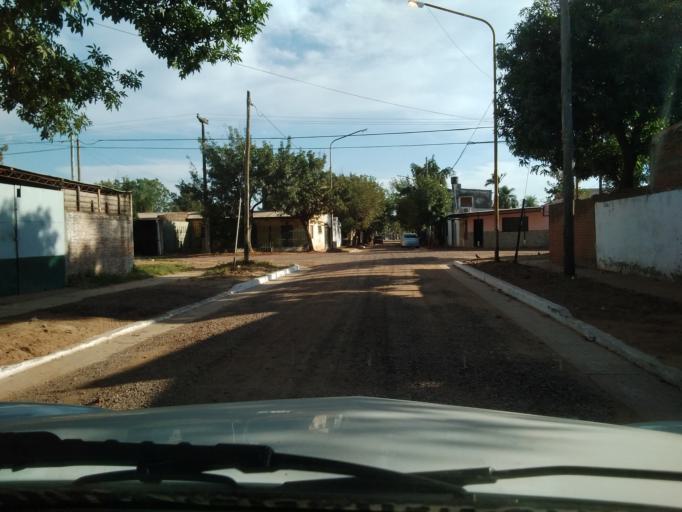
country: AR
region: Corrientes
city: Corrientes
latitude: -27.4873
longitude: -58.7835
